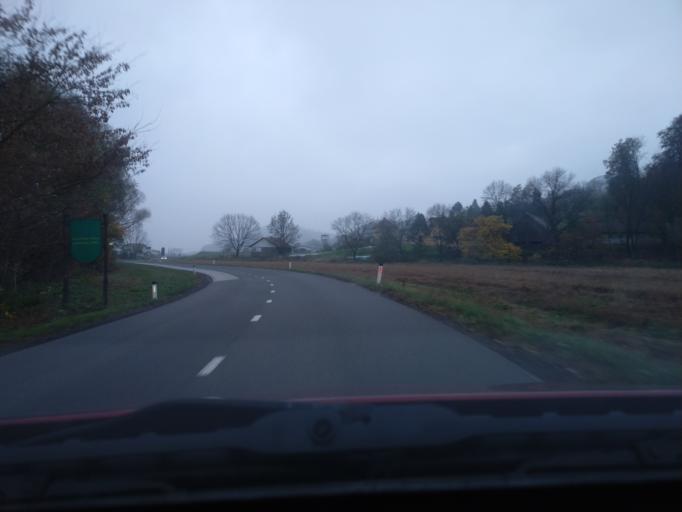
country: SI
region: Pesnica
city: Pesnica pri Mariboru
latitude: 46.6024
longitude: 15.6507
